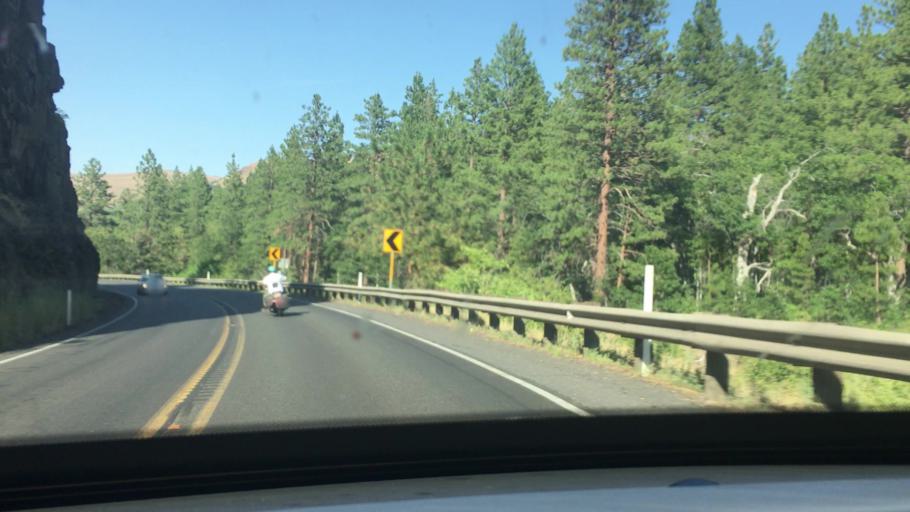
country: US
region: Washington
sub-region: Klickitat County
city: Goldendale
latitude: 46.0389
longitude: -120.5762
